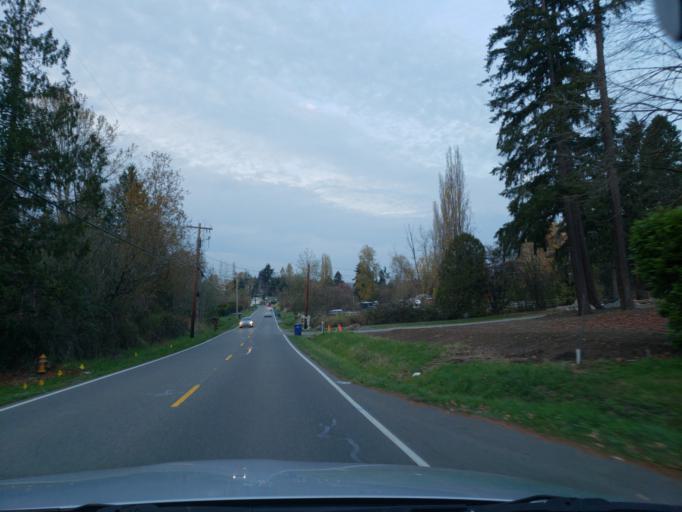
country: US
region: Washington
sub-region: King County
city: Bothell
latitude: 47.7776
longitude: -122.2232
